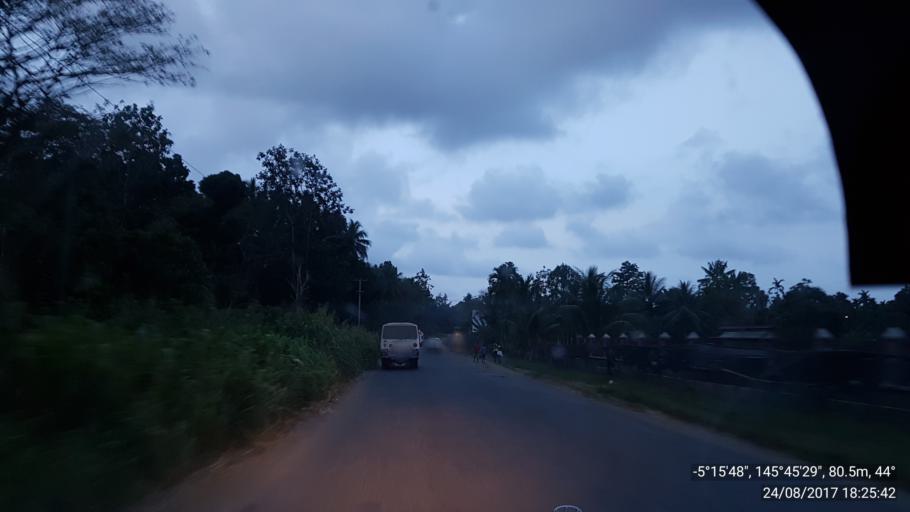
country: PG
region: Madang
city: Madang
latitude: -5.2633
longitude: 145.7581
